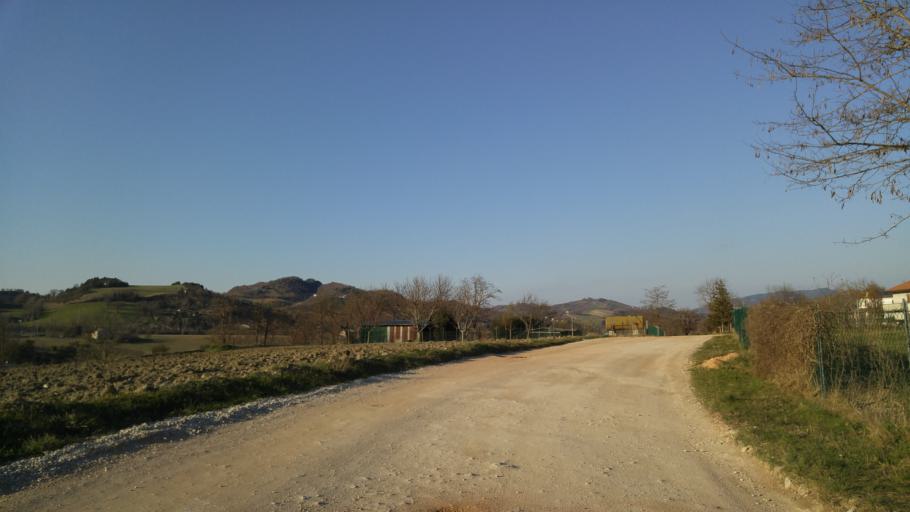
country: IT
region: The Marches
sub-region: Provincia di Pesaro e Urbino
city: Cagli
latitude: 43.5519
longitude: 12.6557
